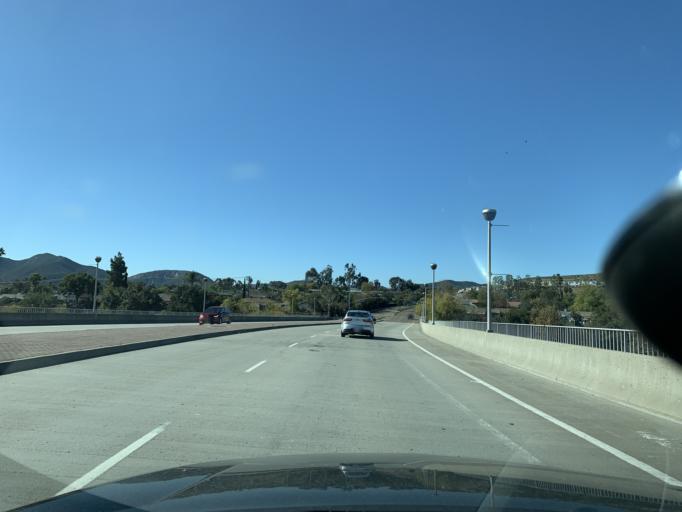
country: US
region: California
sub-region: San Diego County
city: Santee
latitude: 32.8501
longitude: -117.0058
